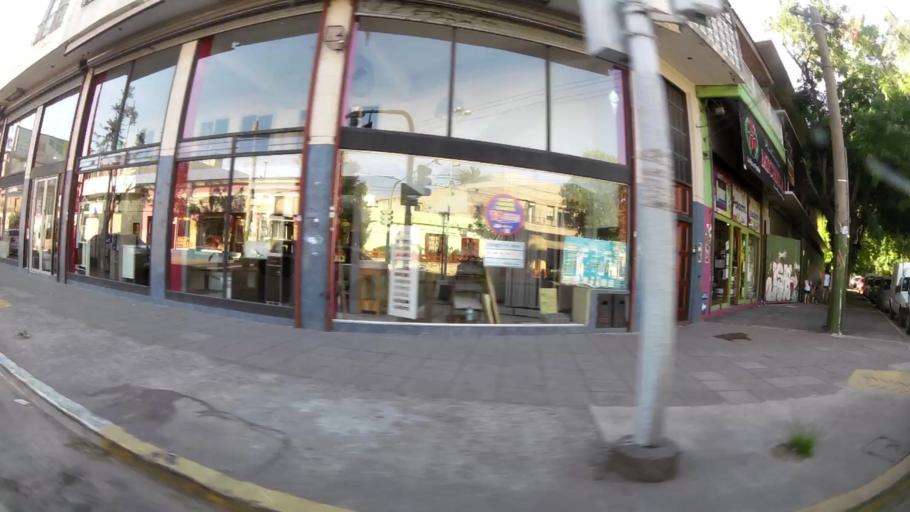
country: AR
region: Buenos Aires
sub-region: Partido de Merlo
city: Merlo
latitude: -34.6743
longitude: -58.7246
